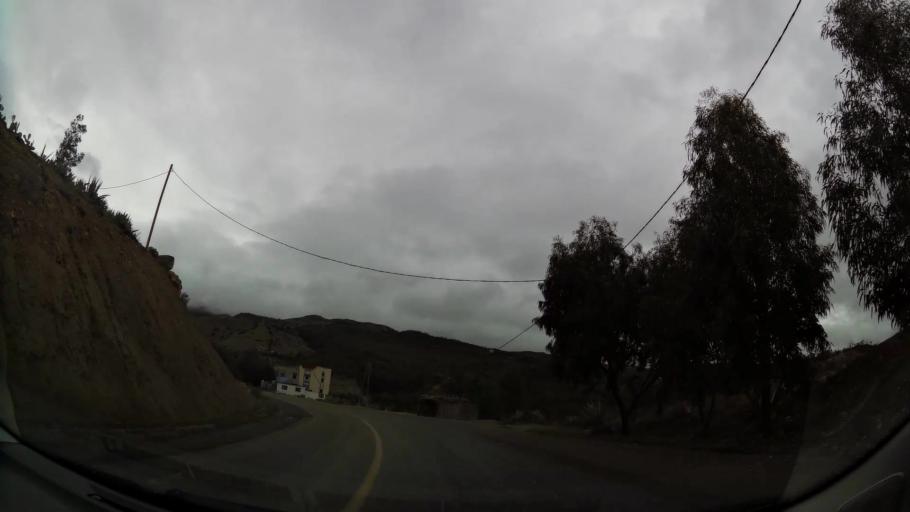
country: MA
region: Taza-Al Hoceima-Taounate
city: Imzourene
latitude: 34.9495
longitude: -3.8086
